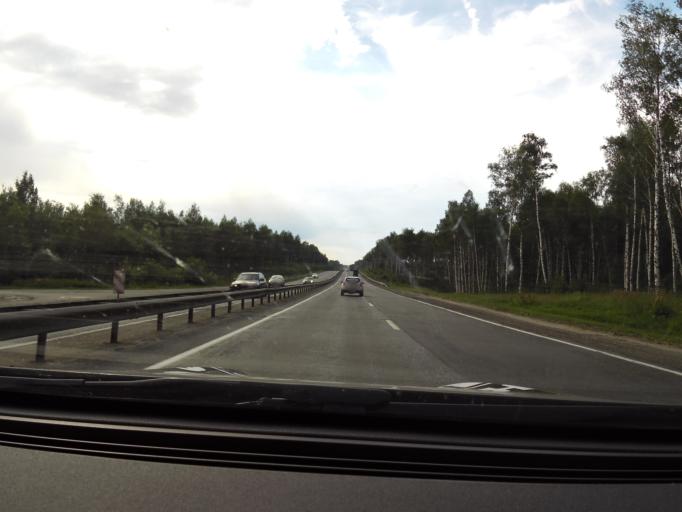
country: RU
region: Vladimir
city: Novovyazniki
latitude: 56.2050
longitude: 42.2869
